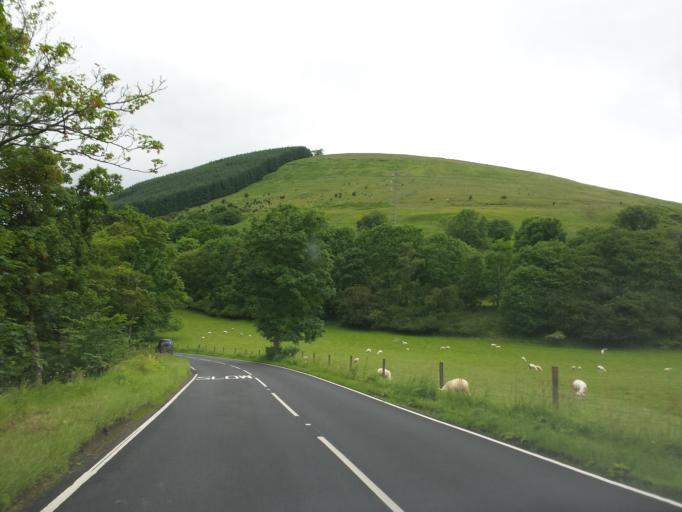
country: GB
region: Scotland
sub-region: Stirling
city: Callander
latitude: 56.3897
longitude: -4.2479
